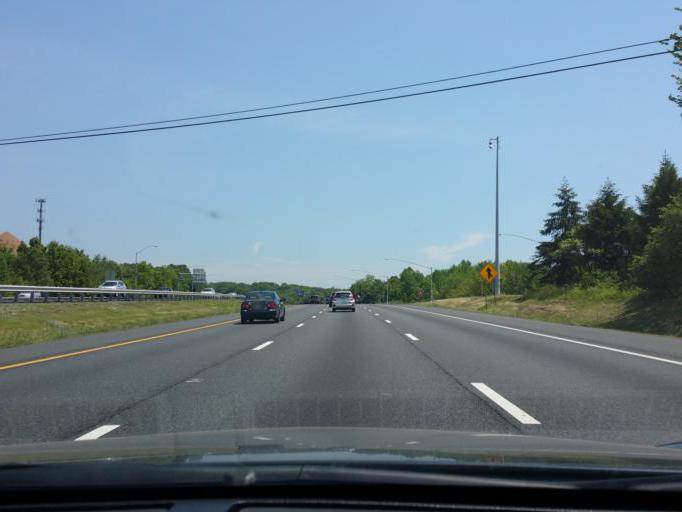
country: US
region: Maryland
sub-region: Harford County
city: Riverside
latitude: 39.4851
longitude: -76.2482
